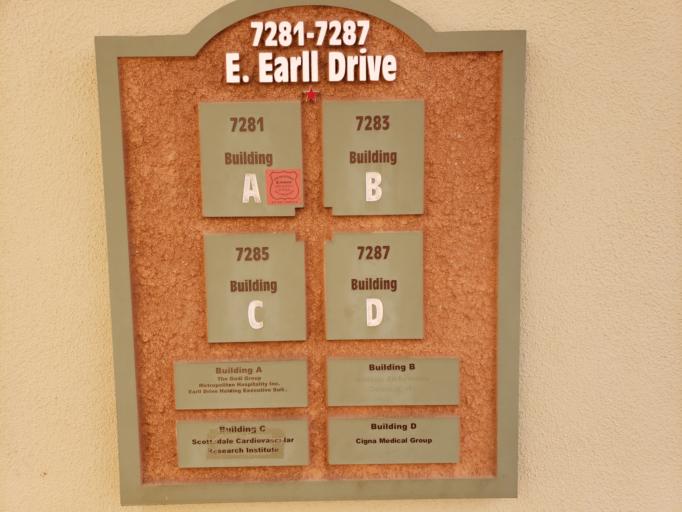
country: US
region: Arizona
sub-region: Maricopa County
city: Scottsdale
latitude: 33.4838
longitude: -111.9245
